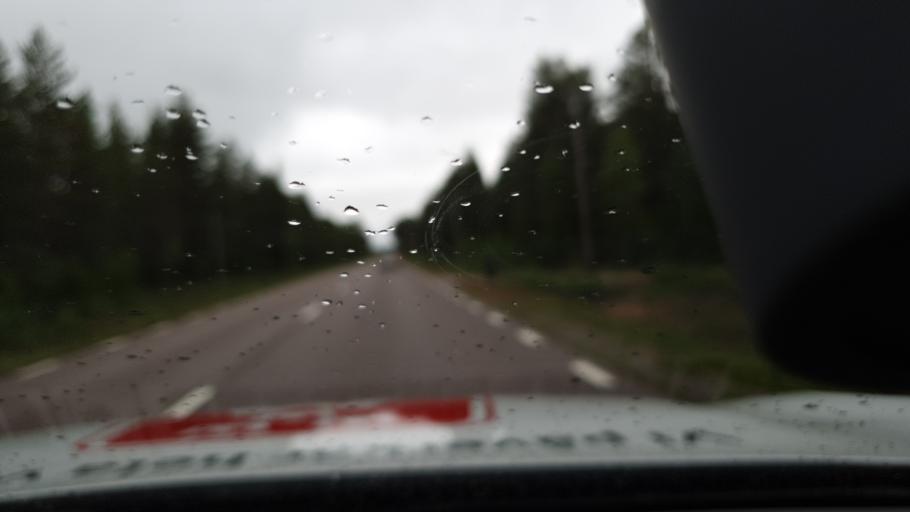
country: FI
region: Lapland
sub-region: Torniolaakso
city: Pello
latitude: 66.9760
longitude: 23.8061
